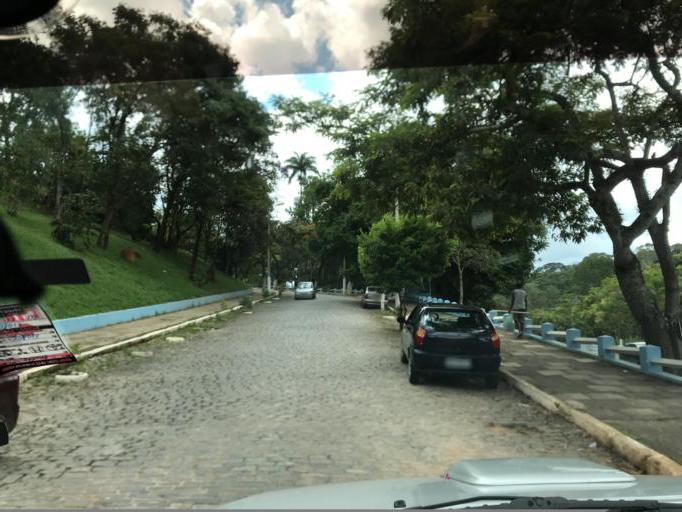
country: BR
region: Minas Gerais
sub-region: Cambuquira
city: Cambuquira
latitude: -21.8536
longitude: -45.2929
